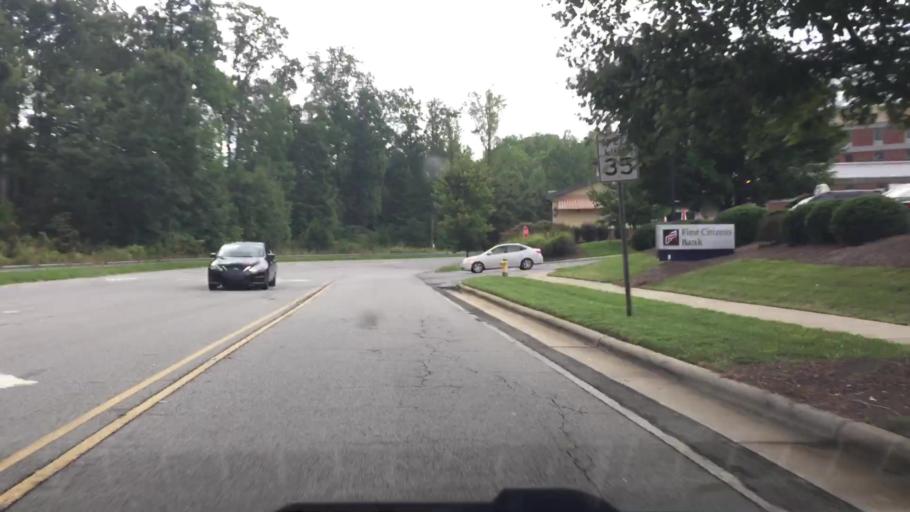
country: US
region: North Carolina
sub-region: Iredell County
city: Mooresville
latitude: 35.5545
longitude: -80.8537
